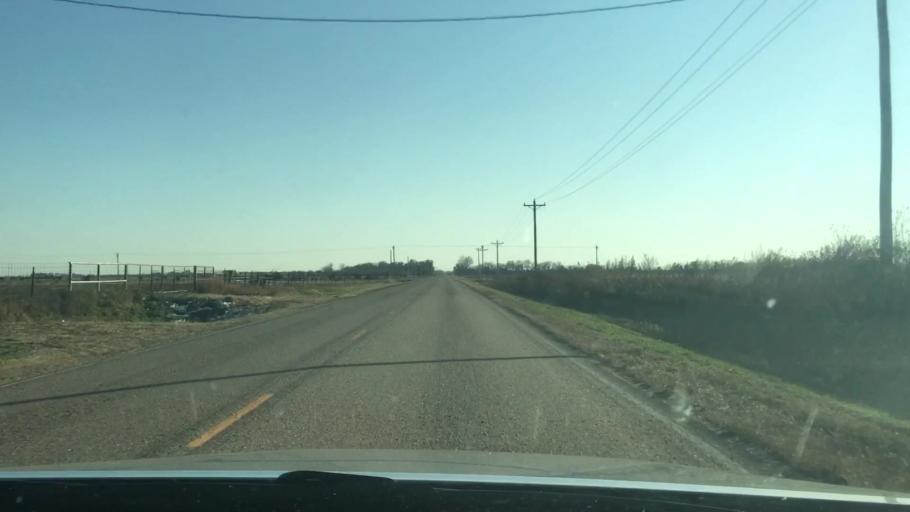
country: US
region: Kansas
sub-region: Reno County
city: Nickerson
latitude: 38.1903
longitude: -98.0876
